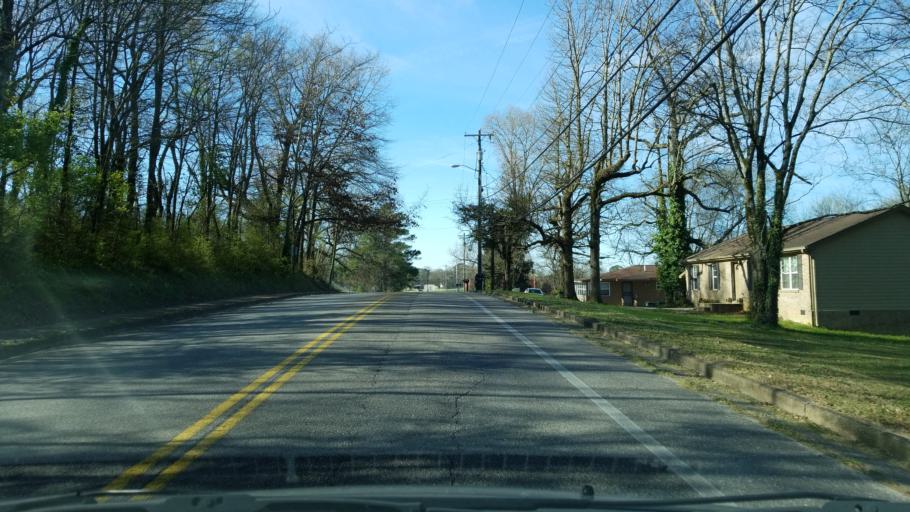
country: US
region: Tennessee
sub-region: Hamilton County
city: East Brainerd
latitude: 35.0461
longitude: -85.1833
